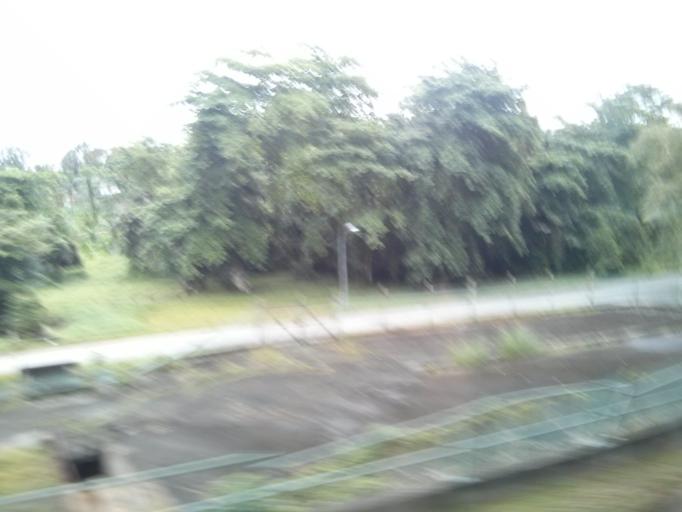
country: SG
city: Singapore
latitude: 1.2858
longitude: 103.7983
